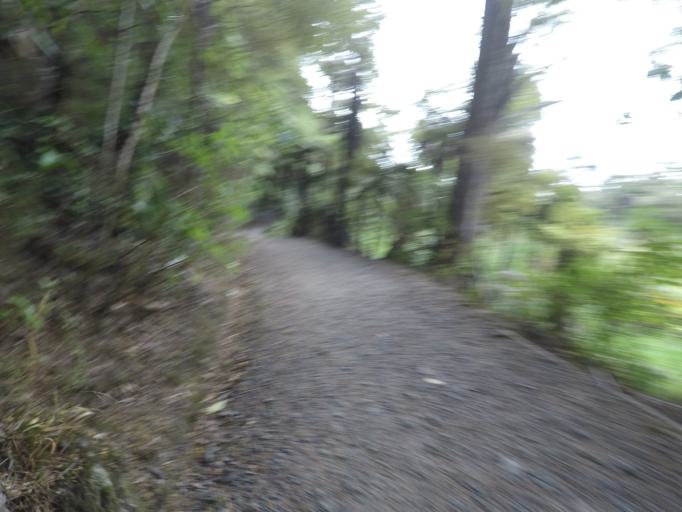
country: NZ
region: Northland
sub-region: Whangarei
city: Whangarei
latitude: -35.7132
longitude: 174.3307
